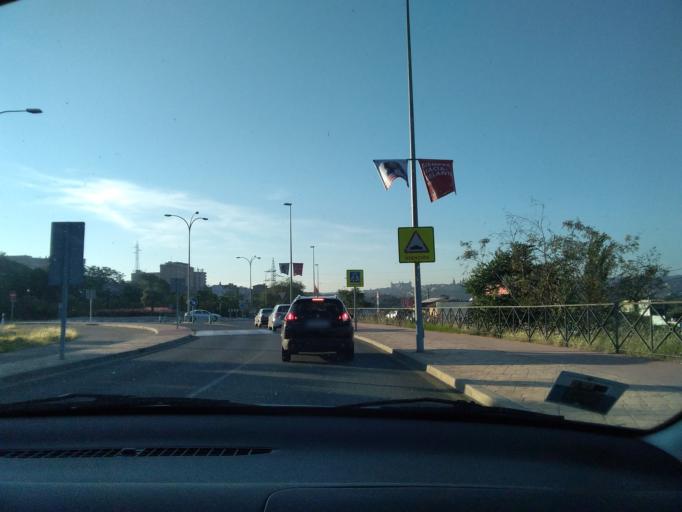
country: ES
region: Castille-La Mancha
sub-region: Province of Toledo
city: Toledo
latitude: 39.8796
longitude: -4.0485
